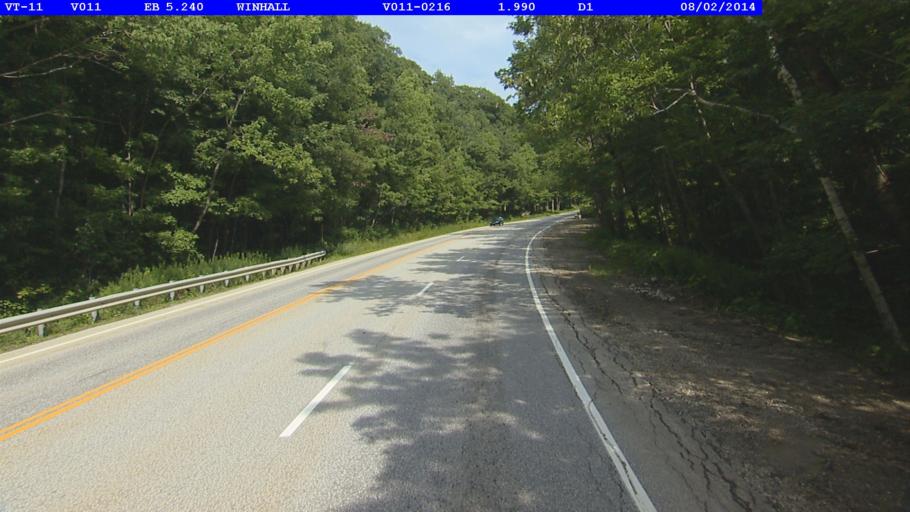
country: US
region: Vermont
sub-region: Bennington County
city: Manchester Center
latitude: 43.2070
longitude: -72.9817
